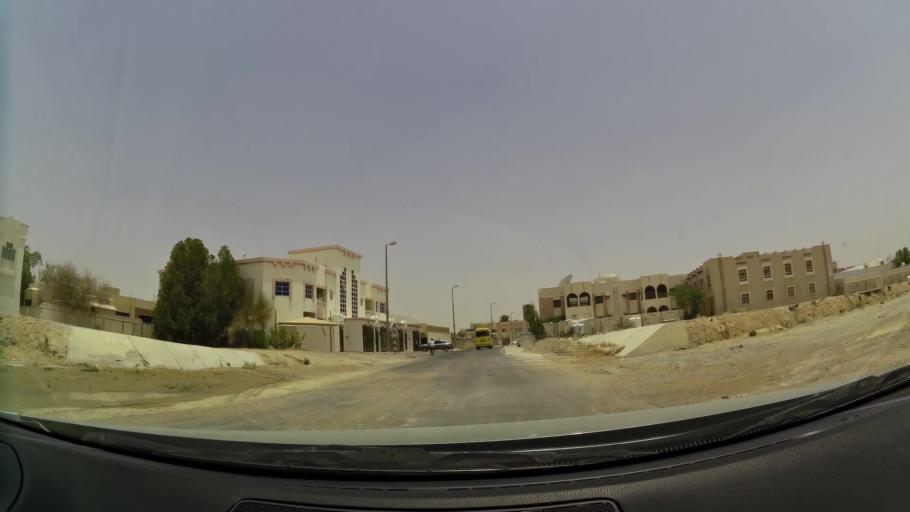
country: AE
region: Abu Dhabi
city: Al Ain
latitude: 24.2091
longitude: 55.7548
